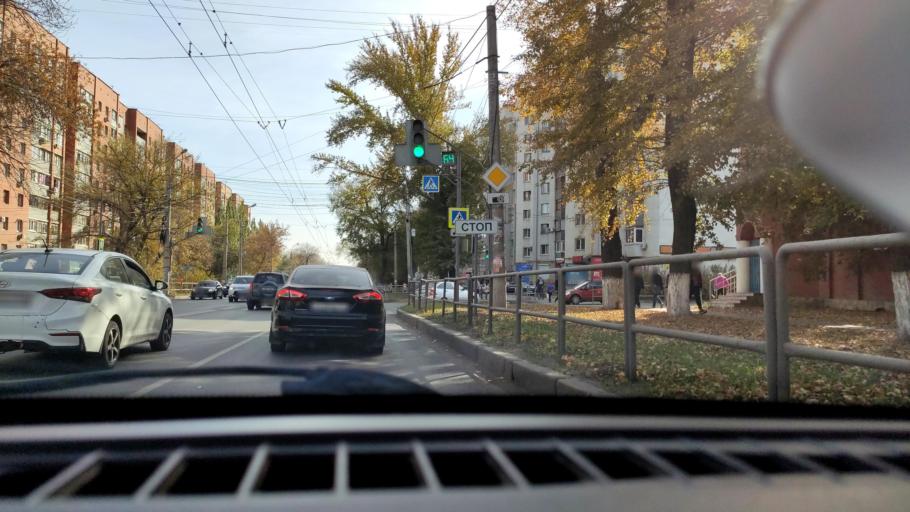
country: RU
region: Samara
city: Samara
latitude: 53.2321
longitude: 50.2464
